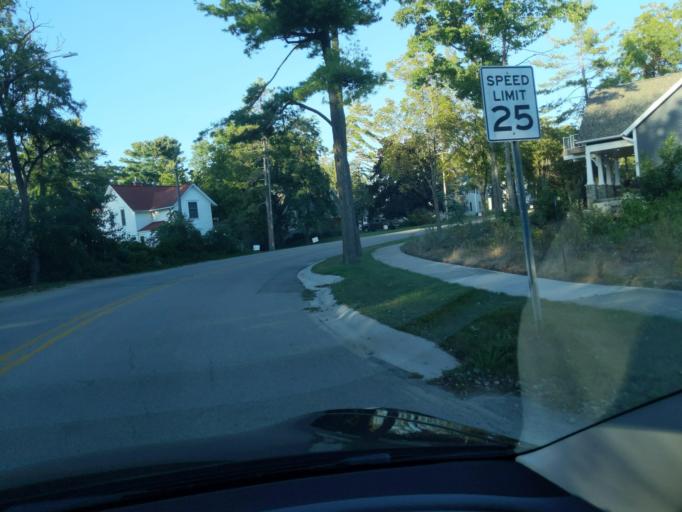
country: US
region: Michigan
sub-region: Antrim County
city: Elk Rapids
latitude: 44.8942
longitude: -85.4224
